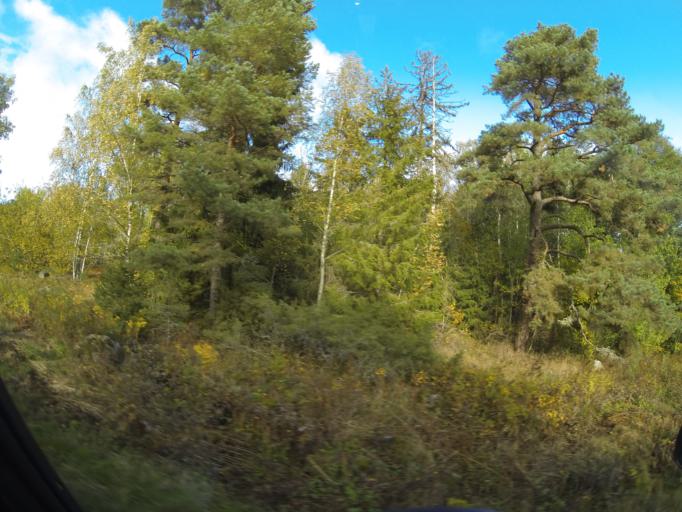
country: SE
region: Soedermanland
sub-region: Eskilstuna Kommun
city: Kvicksund
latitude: 59.3920
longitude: 16.2283
